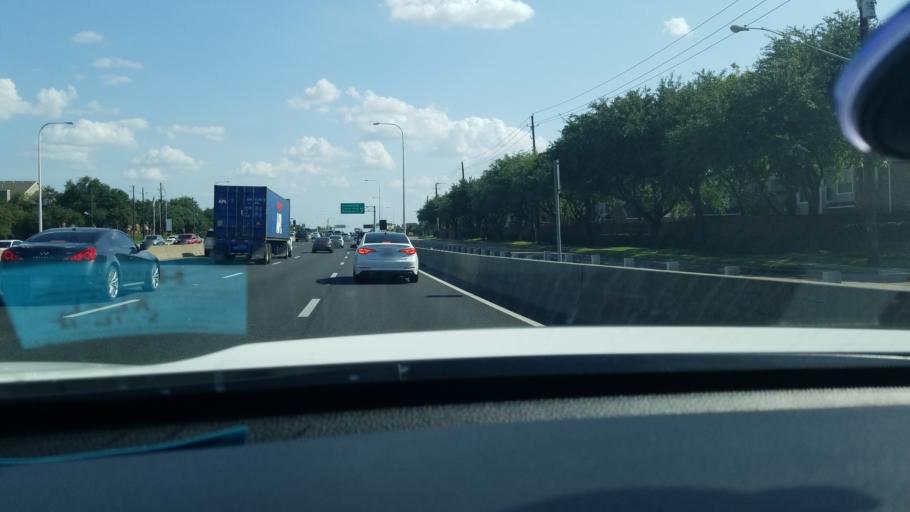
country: US
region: Texas
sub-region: Dallas County
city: Addison
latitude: 33.0048
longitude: -96.8293
